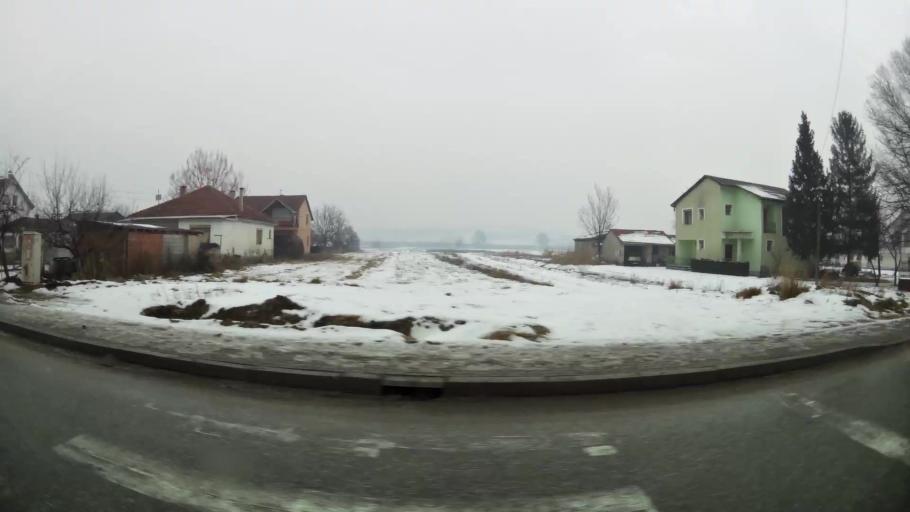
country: MK
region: Petrovec
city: Petrovec
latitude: 41.9328
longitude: 21.6229
